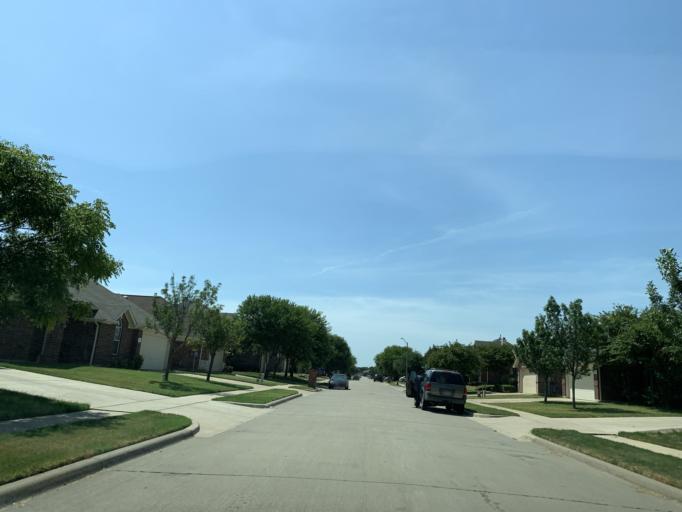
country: US
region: Texas
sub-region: Dallas County
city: Cedar Hill
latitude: 32.6437
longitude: -97.0171
